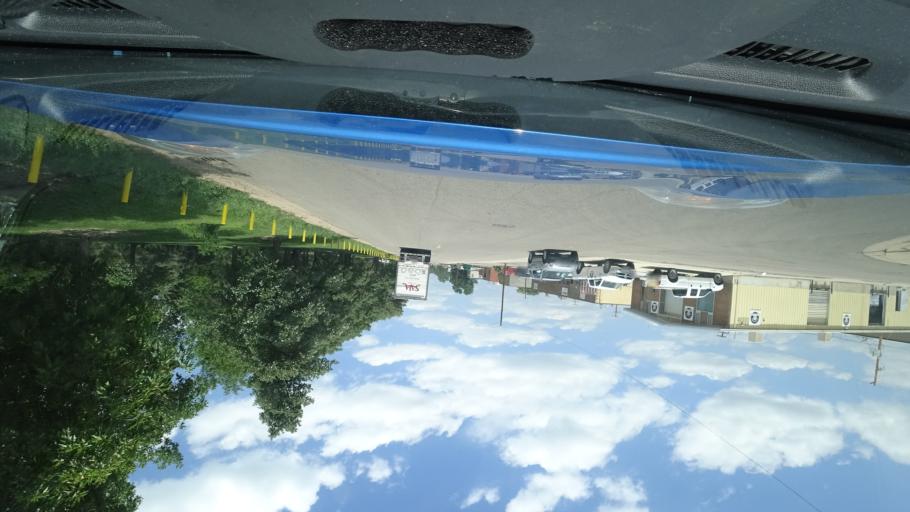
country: US
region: Colorado
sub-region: Arapahoe County
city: Englewood
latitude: 39.6728
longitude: -104.9981
